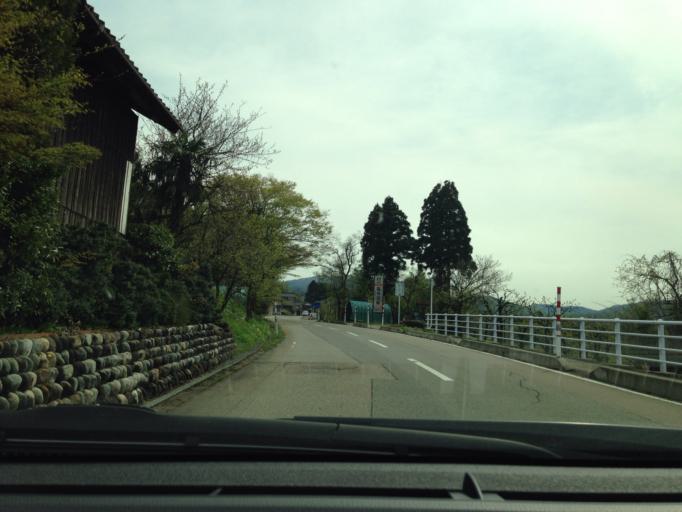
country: JP
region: Toyama
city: Fukumitsu
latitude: 36.5253
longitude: 136.8606
